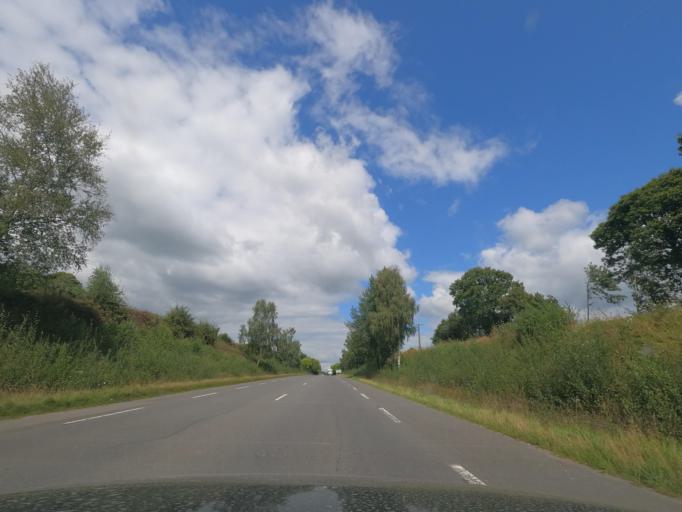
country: FR
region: Brittany
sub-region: Departement d'Ille-et-Vilaine
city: Lecousse
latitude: 48.3601
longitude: -1.2289
